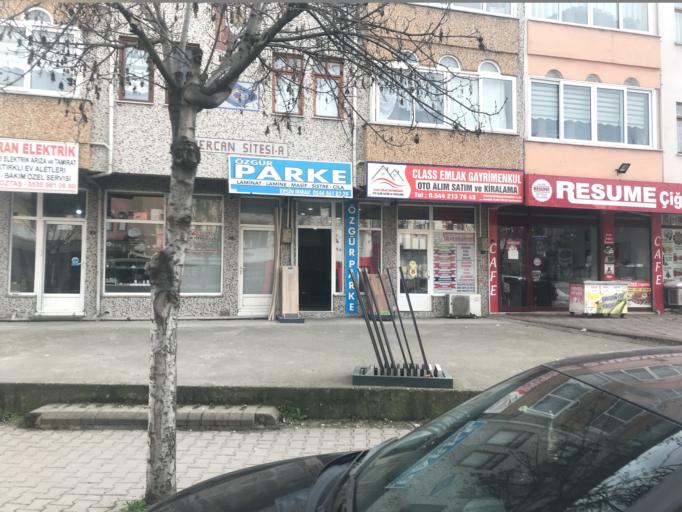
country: TR
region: Karabuk
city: Safranbolu
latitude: 41.2497
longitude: 32.6797
